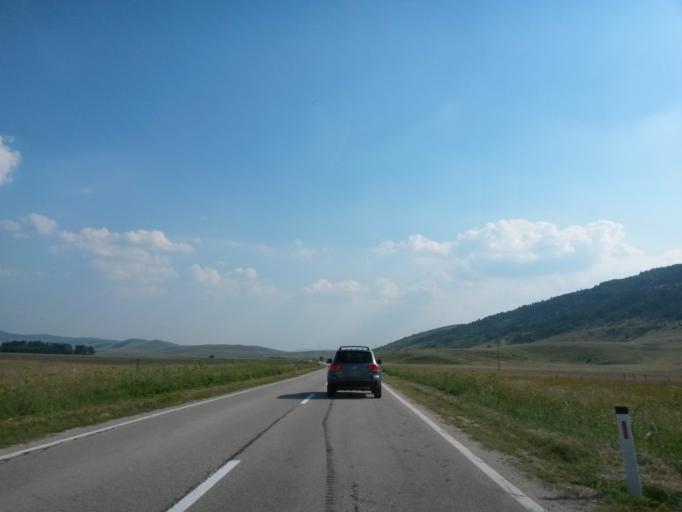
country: BA
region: Federation of Bosnia and Herzegovina
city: Tomislavgrad
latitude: 43.9253
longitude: 17.2072
